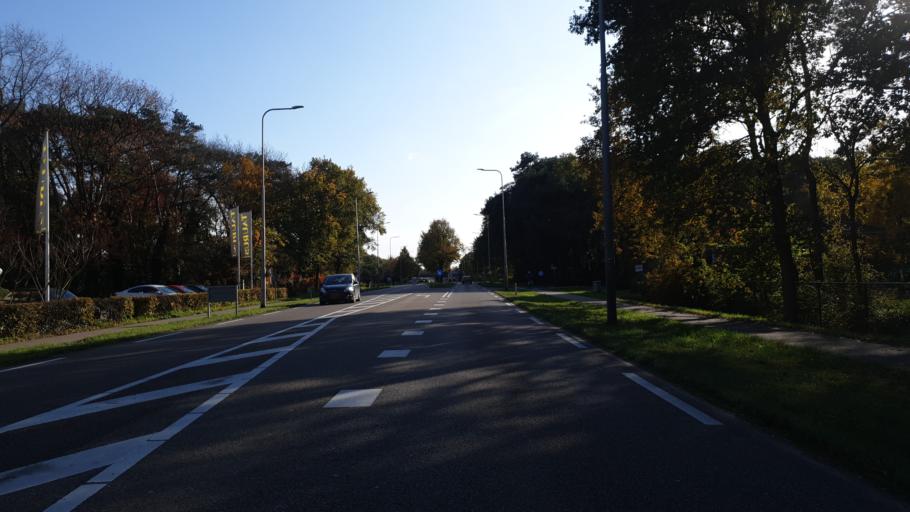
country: NL
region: Limburg
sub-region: Gemeente Venlo
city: Venlo
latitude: 51.4000
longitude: 6.1704
